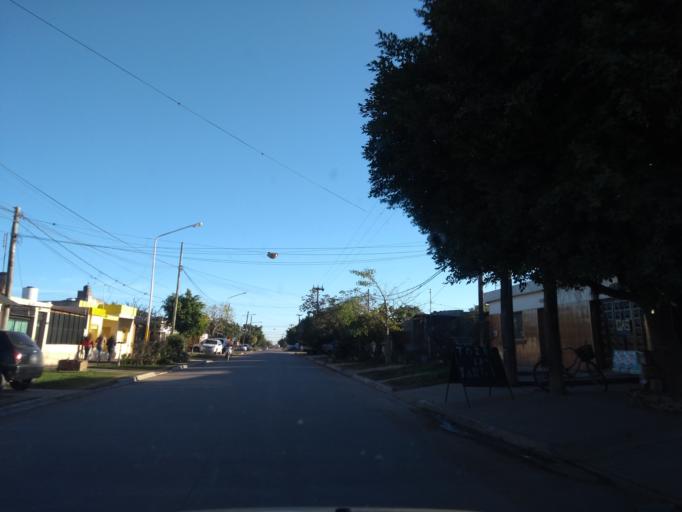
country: AR
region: Chaco
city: Barranqueras
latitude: -27.4902
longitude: -58.9479
